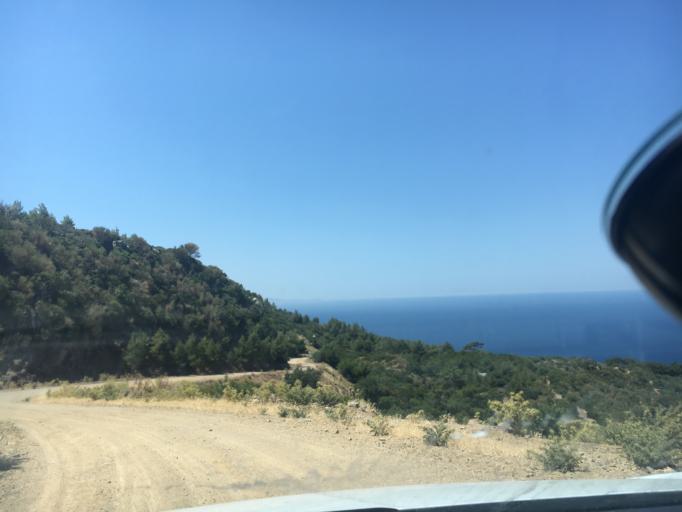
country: TR
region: Canakkale
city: Gulpinar
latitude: 39.4874
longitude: 26.0790
